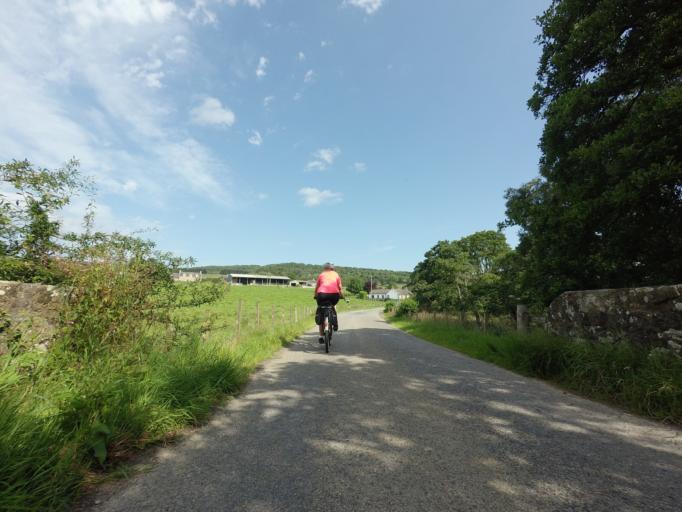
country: GB
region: Scotland
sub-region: Highland
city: Invergordon
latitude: 57.7515
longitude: -4.1602
